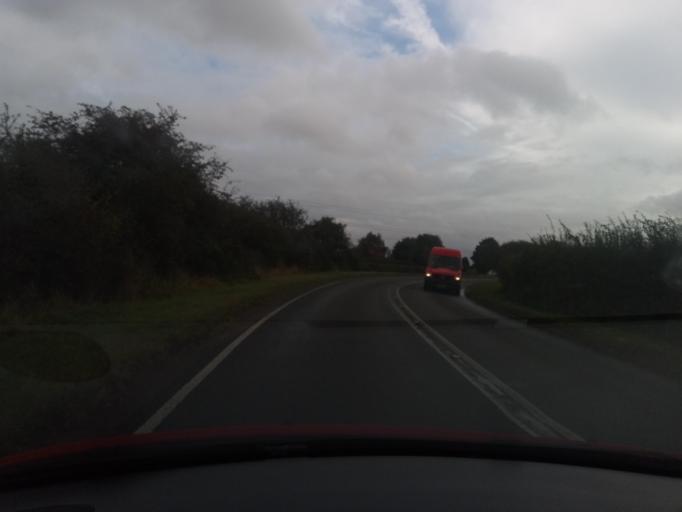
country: GB
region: England
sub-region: Nottinghamshire
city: Cotgrave
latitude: 52.9247
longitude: -1.0239
